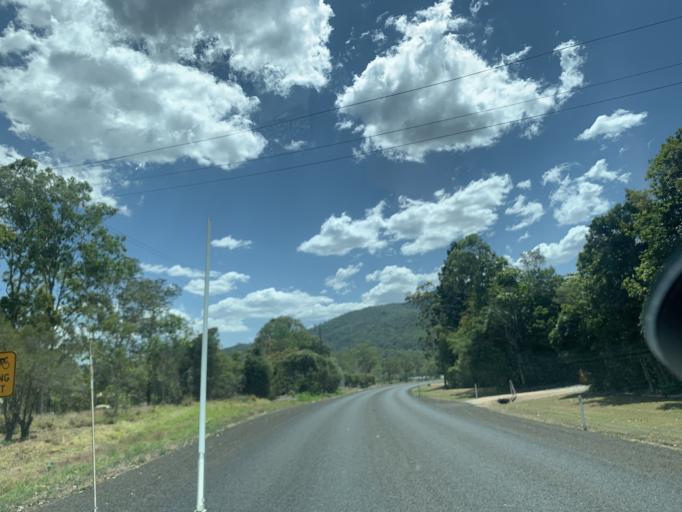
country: AU
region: Queensland
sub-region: Tablelands
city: Atherton
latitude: -17.3038
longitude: 145.4658
